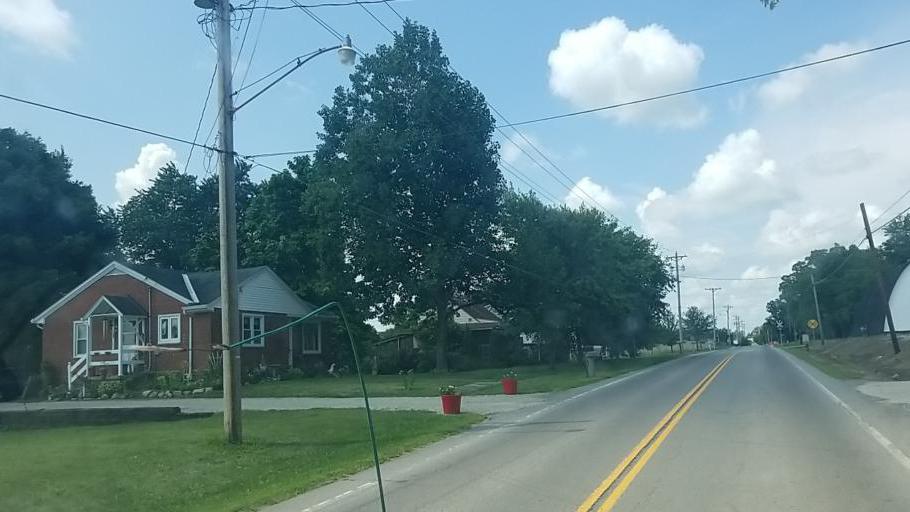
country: US
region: Ohio
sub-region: Wayne County
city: West Salem
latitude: 40.9712
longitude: -82.1034
